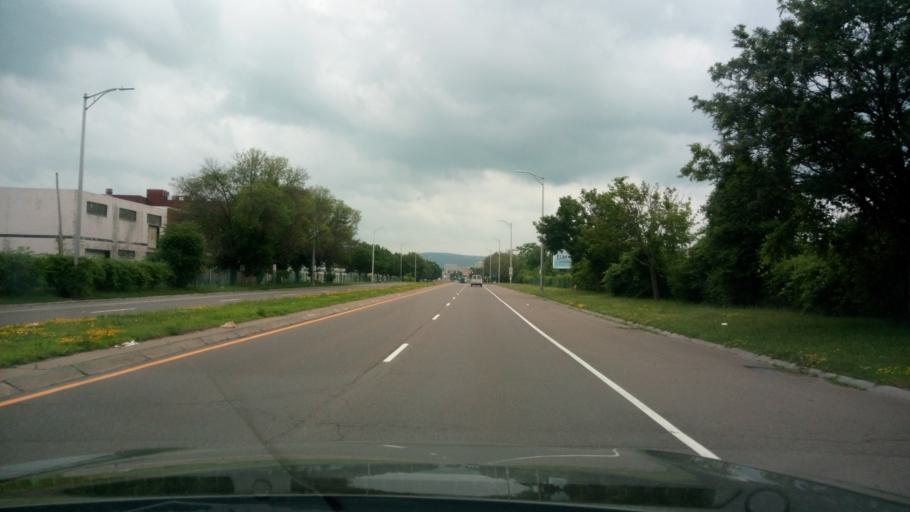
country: US
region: New York
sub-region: Chemung County
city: Elmira
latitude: 42.0953
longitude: -76.8073
